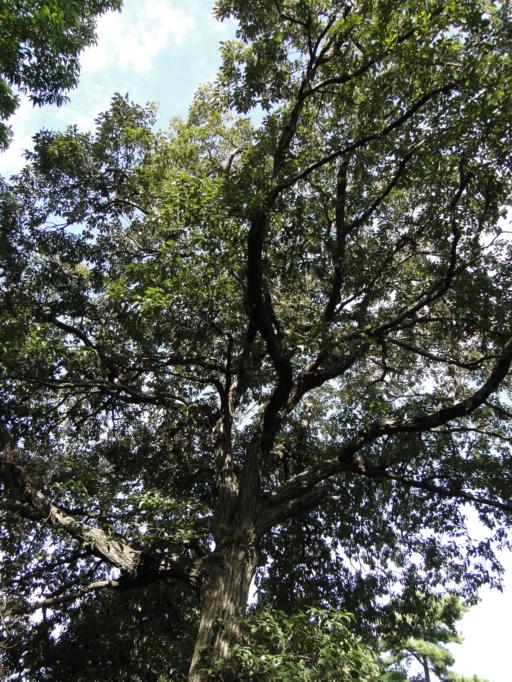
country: JP
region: Kanagawa
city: Yokohama
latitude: 35.4160
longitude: 139.6590
